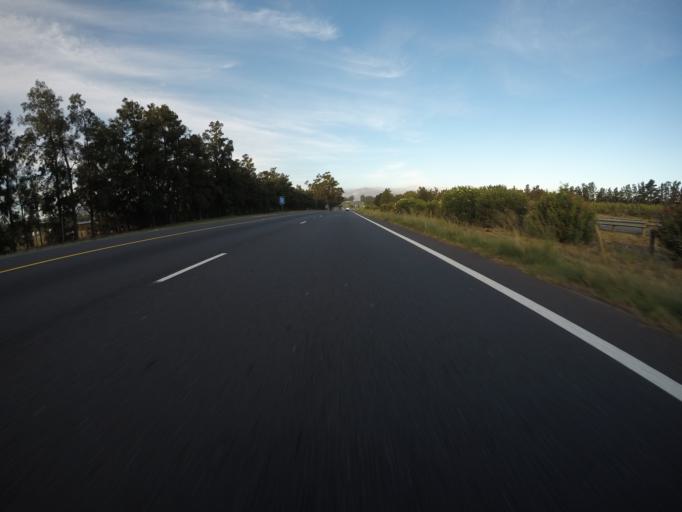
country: ZA
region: Western Cape
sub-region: Cape Winelands District Municipality
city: Paarl
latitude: -33.7998
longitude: 18.8634
